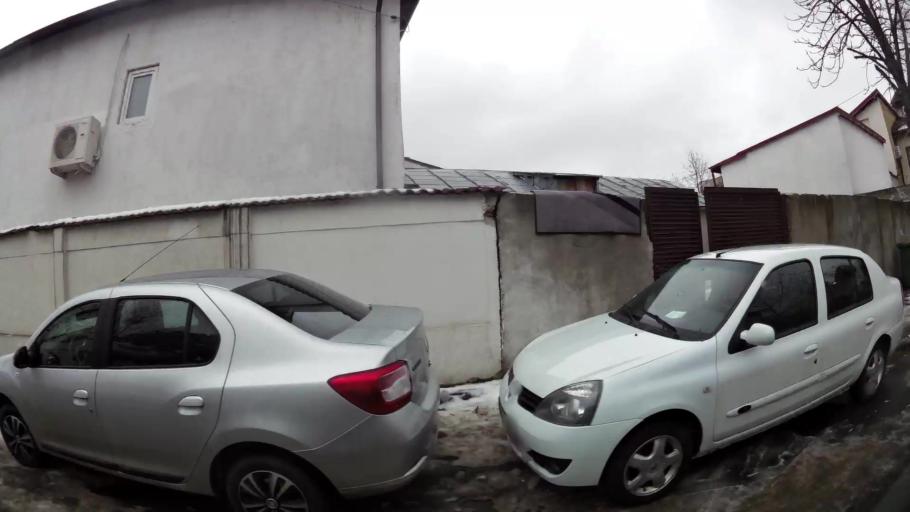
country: RO
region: Ilfov
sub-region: Comuna Chiajna
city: Rosu
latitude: 44.4825
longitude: 26.0371
